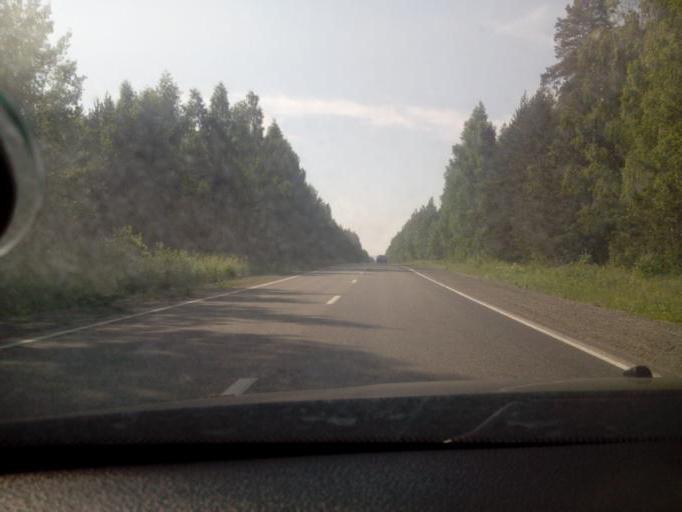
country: RU
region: Sverdlovsk
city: Iset'
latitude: 57.1102
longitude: 60.3413
